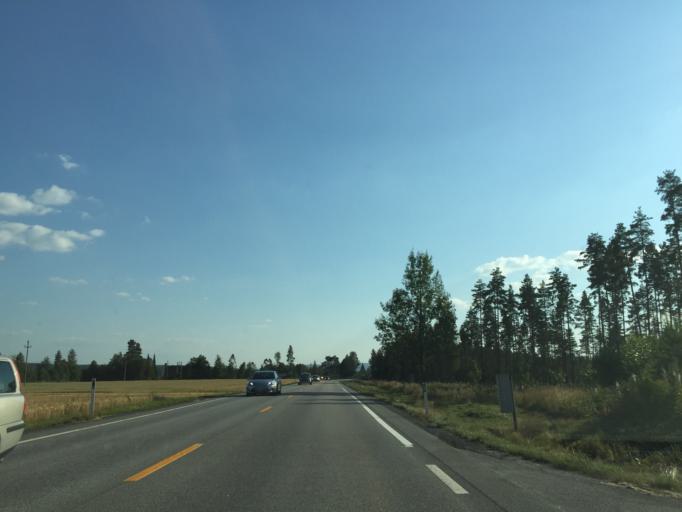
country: NO
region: Hedmark
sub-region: Sor-Odal
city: Skarnes
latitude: 60.2330
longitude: 11.6675
